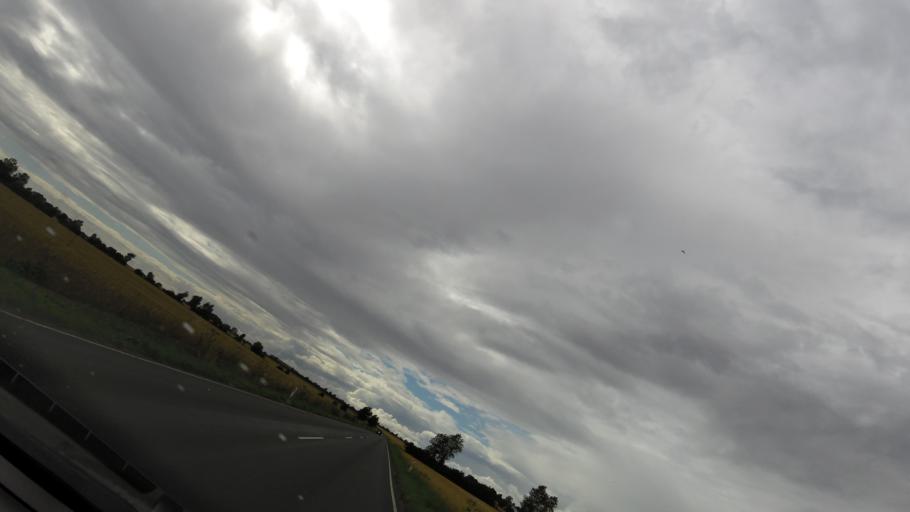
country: DK
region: South Denmark
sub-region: Nordfyns Kommune
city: Otterup
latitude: 55.4845
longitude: 10.3734
